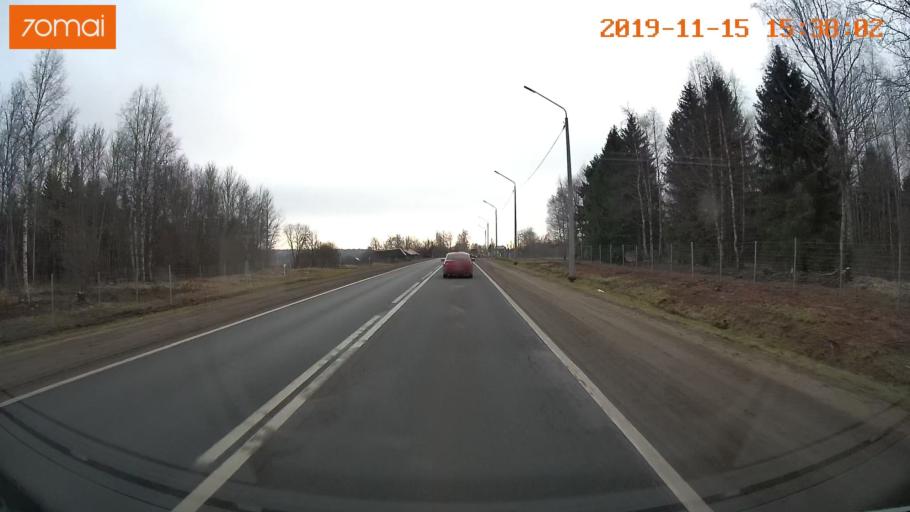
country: RU
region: Jaroslavl
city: Danilov
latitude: 58.0334
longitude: 40.0843
